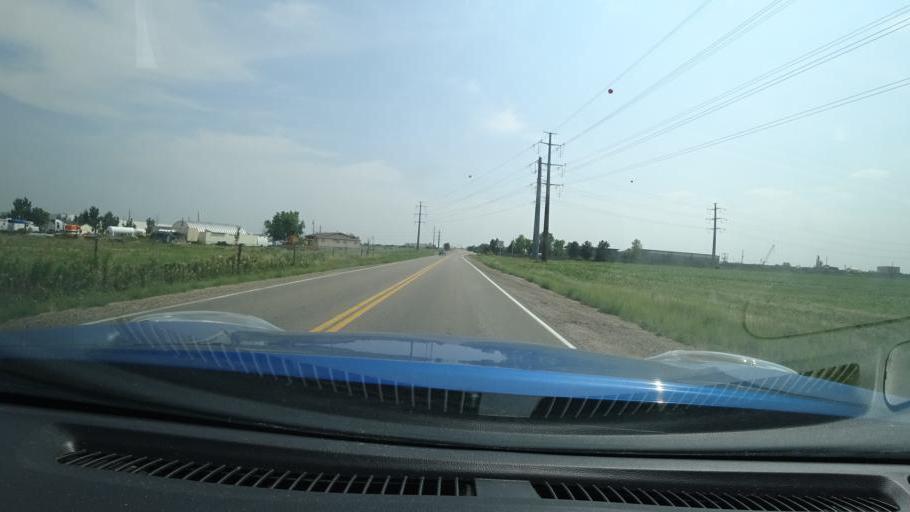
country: US
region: Colorado
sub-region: Adams County
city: Aurora
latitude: 39.7562
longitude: -104.7347
